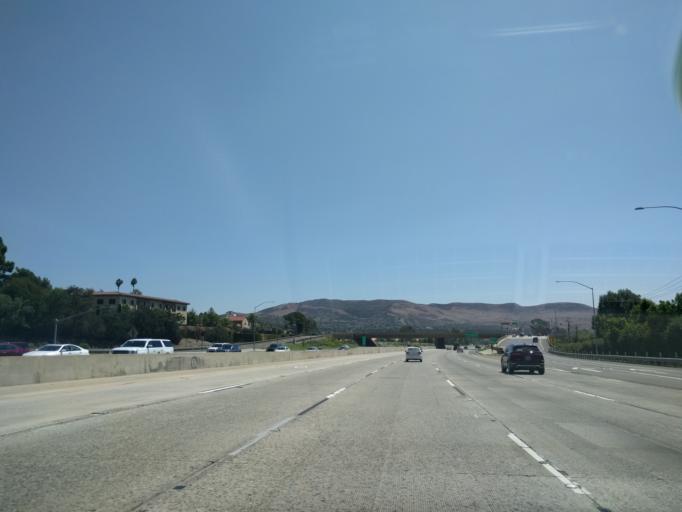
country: US
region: California
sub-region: Orange County
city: San Juan Capistrano
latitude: 33.5052
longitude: -117.6594
